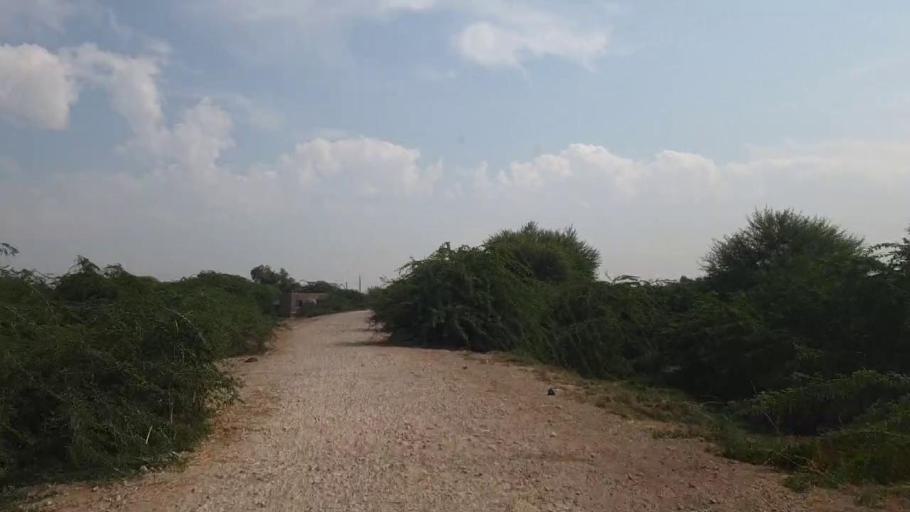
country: PK
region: Sindh
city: Tando Bago
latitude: 24.9340
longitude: 69.0031
